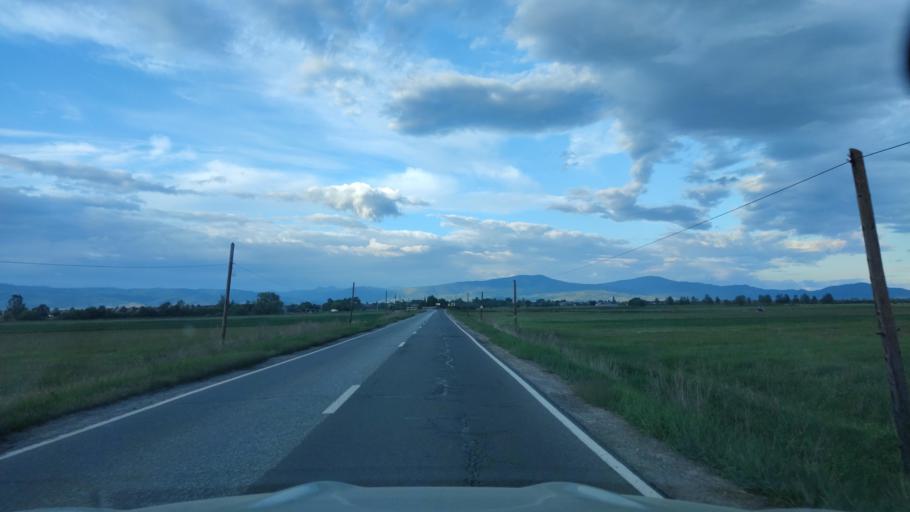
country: RO
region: Harghita
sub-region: Comuna Joseni
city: Joseni
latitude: 46.6976
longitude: 25.4797
